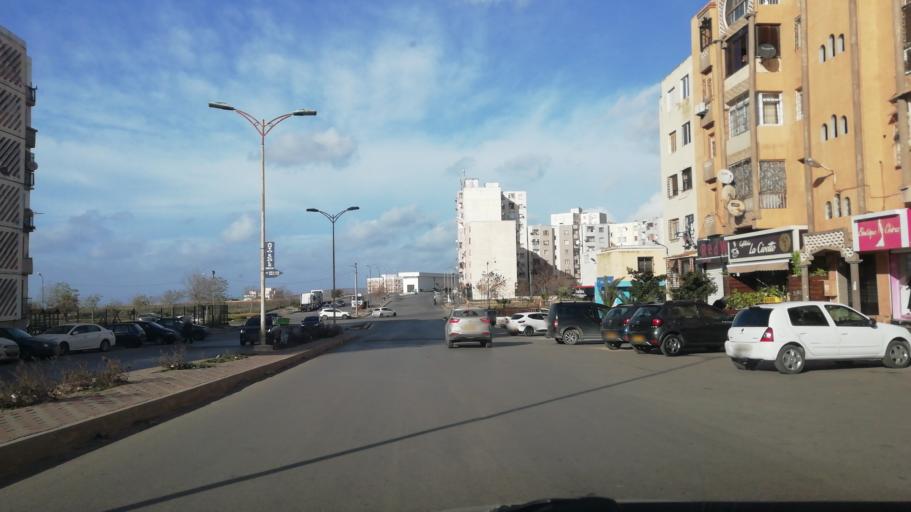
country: DZ
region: Oran
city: Bir el Djir
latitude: 35.7192
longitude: -0.5960
